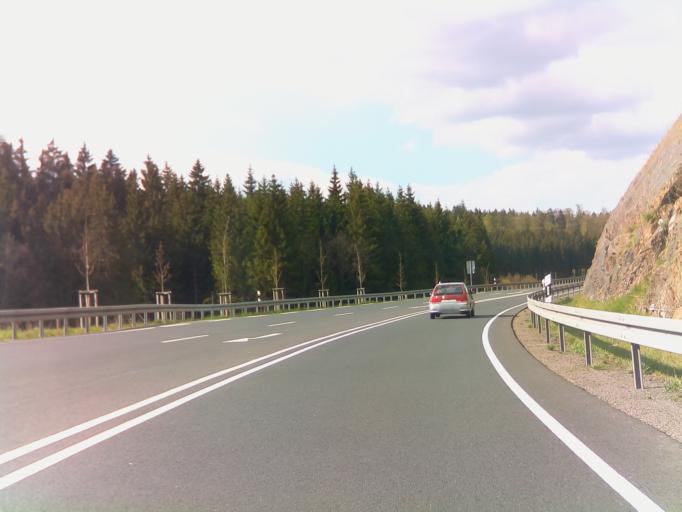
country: DE
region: Bavaria
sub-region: Upper Franconia
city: Teuschnitz
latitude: 50.4173
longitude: 11.3538
